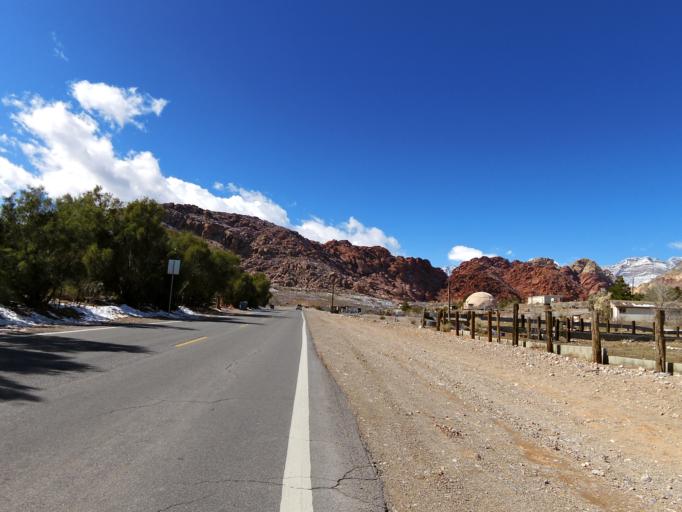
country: US
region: Nevada
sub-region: Clark County
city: Summerlin South
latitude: 36.1473
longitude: -115.4116
